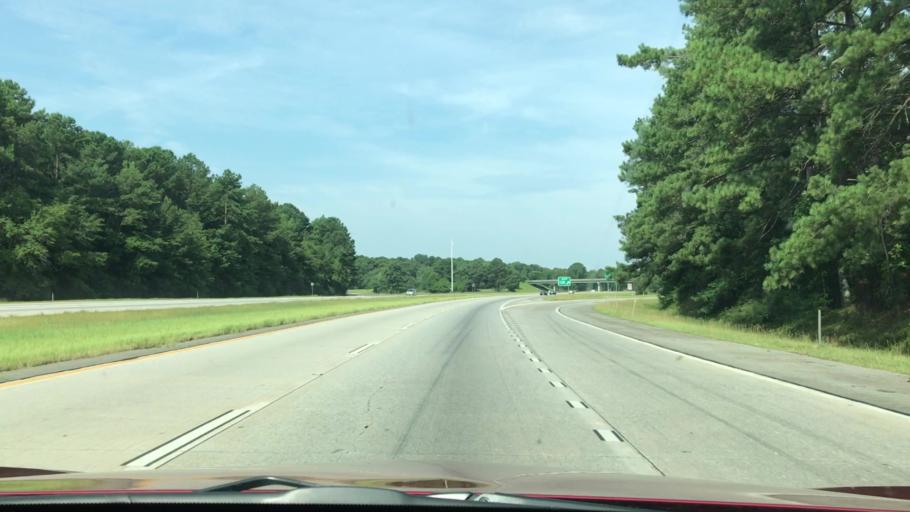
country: US
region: Georgia
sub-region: Greene County
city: Union Point
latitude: 33.5448
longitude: -83.0744
